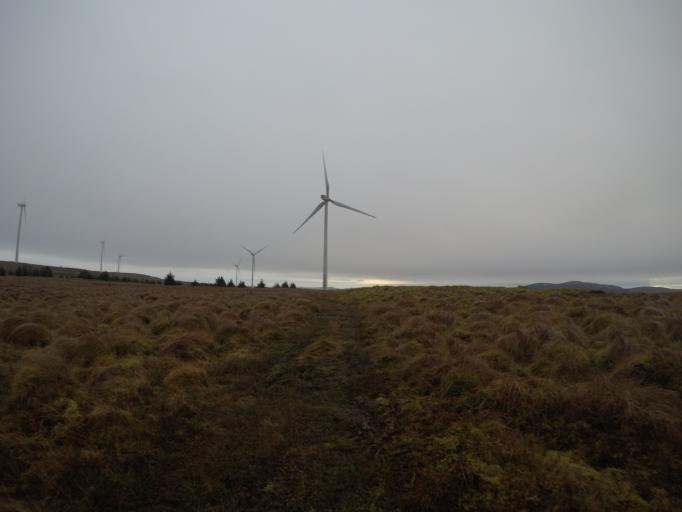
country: GB
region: Scotland
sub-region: North Ayrshire
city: Fairlie
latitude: 55.7386
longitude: -4.7888
